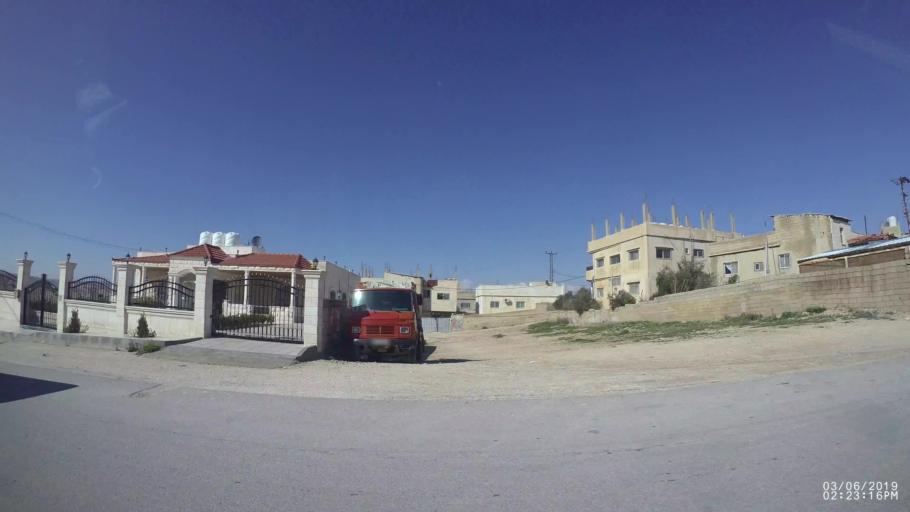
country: JO
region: Zarqa
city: Russeifa
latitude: 32.0421
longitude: 36.0460
